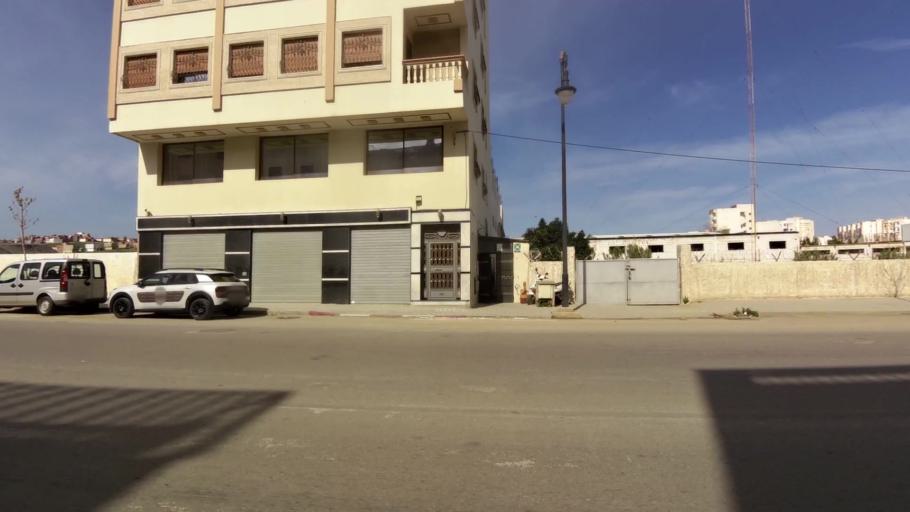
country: MA
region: Tanger-Tetouan
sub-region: Tanger-Assilah
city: Tangier
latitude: 35.7209
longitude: -5.8044
